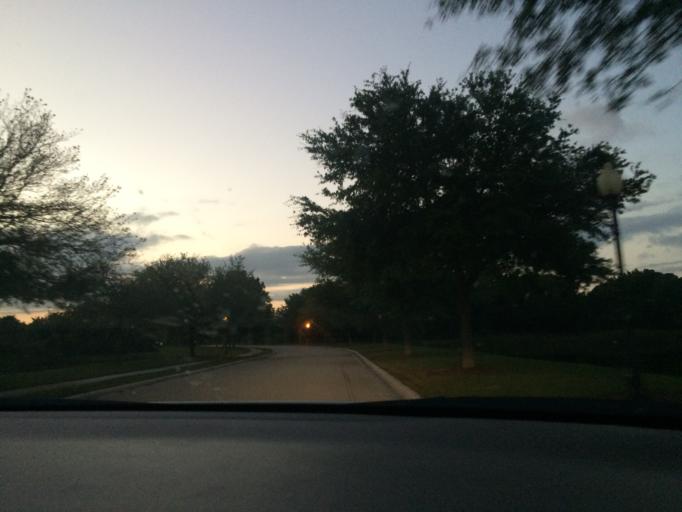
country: US
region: Florida
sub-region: Manatee County
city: Ellenton
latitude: 27.4951
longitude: -82.4123
